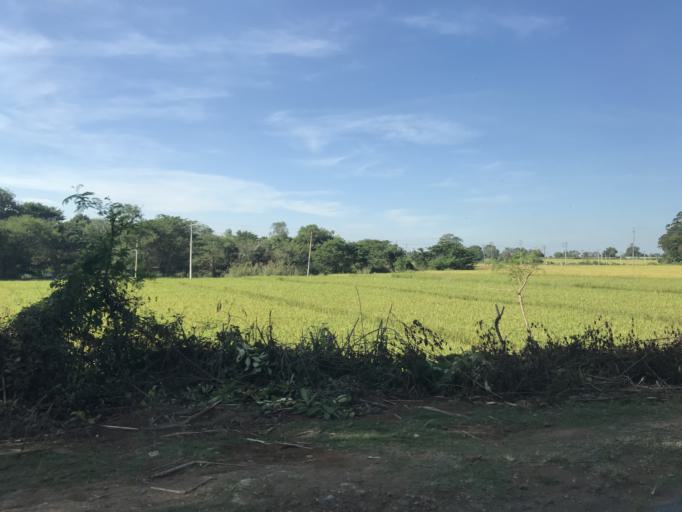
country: IN
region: Karnataka
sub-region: Mysore
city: Heggadadevankote
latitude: 12.1263
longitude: 76.4537
